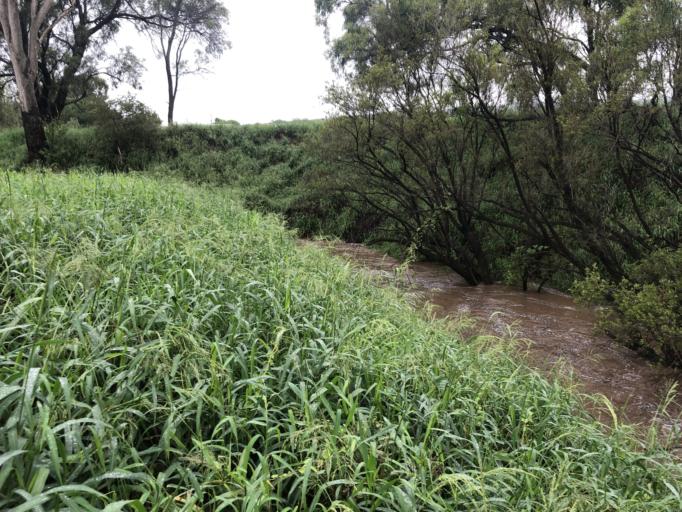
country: AU
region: Queensland
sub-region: Lockyer Valley
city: Gatton
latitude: -27.5894
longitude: 152.3451
